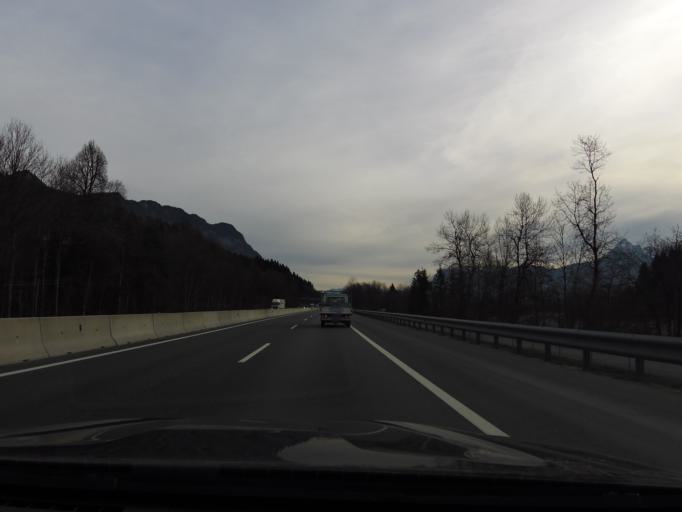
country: AT
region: Tyrol
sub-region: Politischer Bezirk Kufstein
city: Mariastein
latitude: 47.5236
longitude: 12.0716
